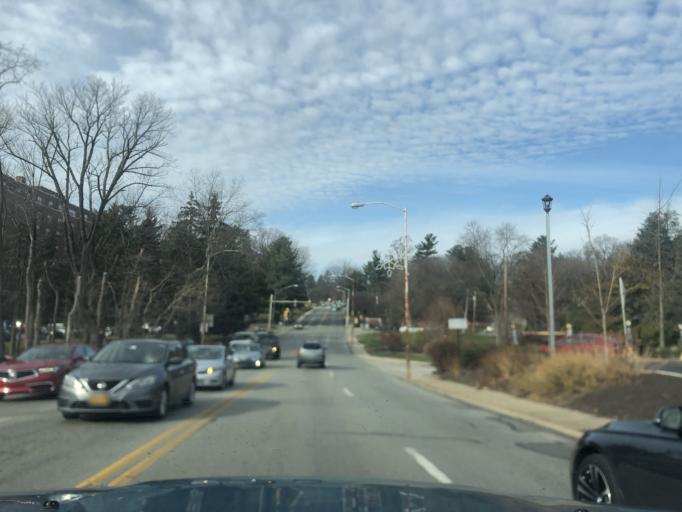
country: US
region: Pennsylvania
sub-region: Montgomery County
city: Bryn Mawr
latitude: 40.0265
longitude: -75.3285
